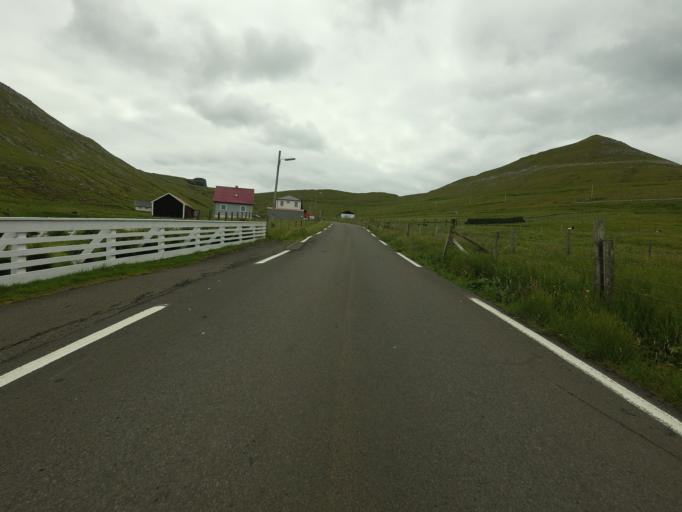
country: FO
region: Suduroy
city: Vagur
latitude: 61.4422
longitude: -6.7712
